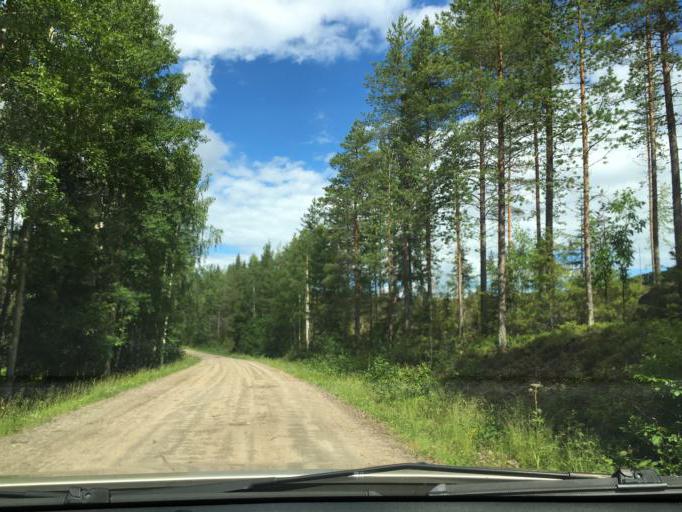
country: SE
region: Norrbotten
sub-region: Overkalix Kommun
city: OEverkalix
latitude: 66.1309
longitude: 22.7848
